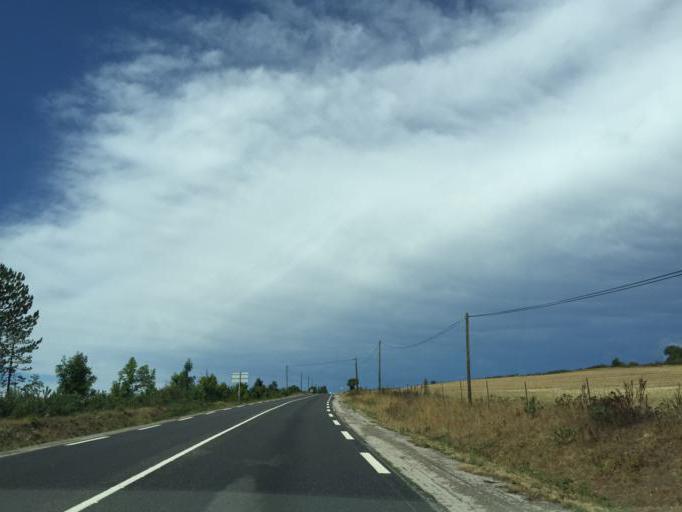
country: FR
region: Midi-Pyrenees
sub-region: Departement de l'Aveyron
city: Millau
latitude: 44.2011
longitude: 3.0158
